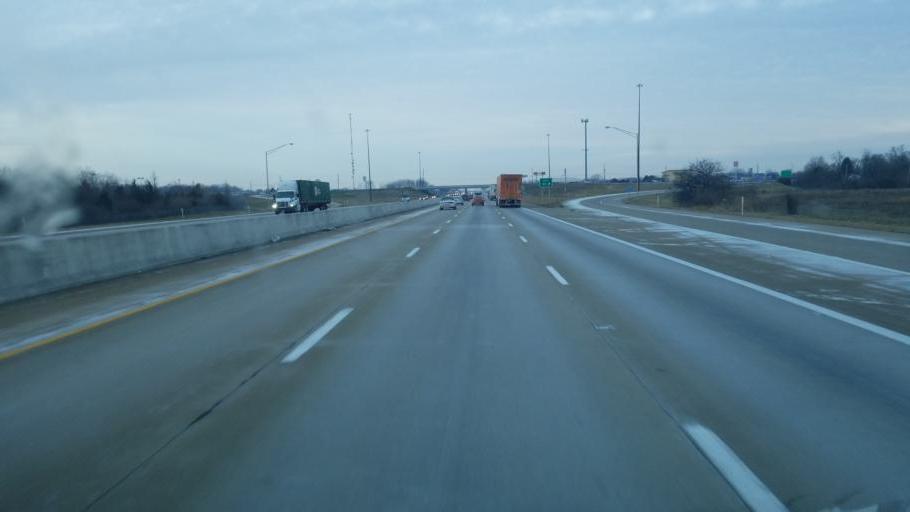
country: US
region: Indiana
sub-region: Marion County
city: Lawrence
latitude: 39.8012
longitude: -86.0040
